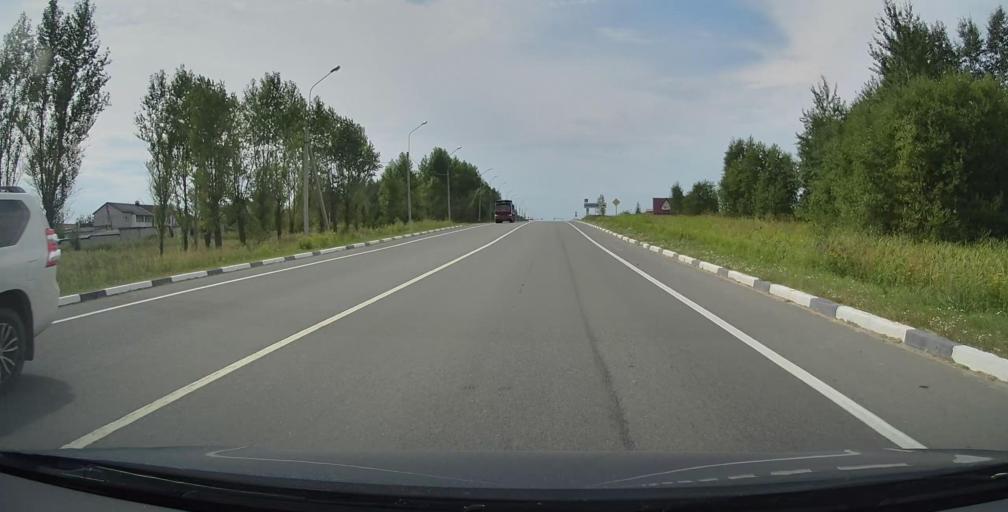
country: RU
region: Jaroslavl
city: Pesochnoye
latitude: 57.9861
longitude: 39.1219
